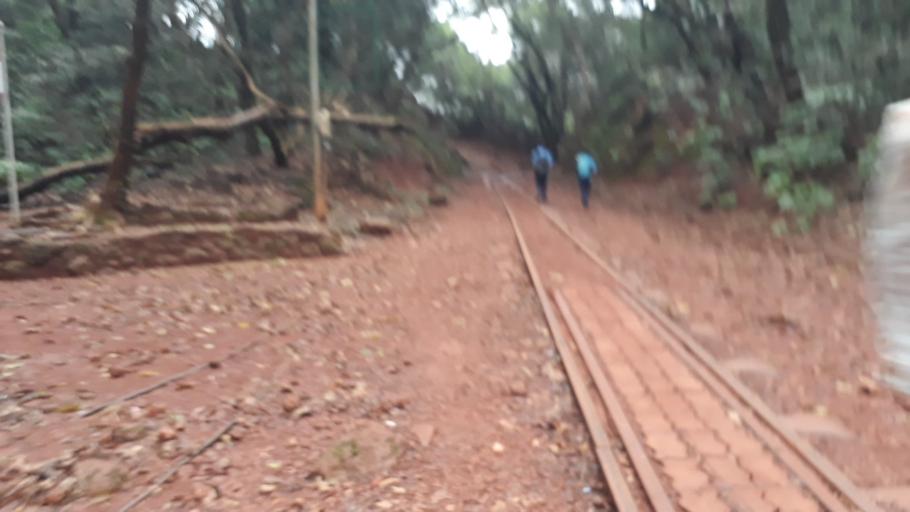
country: IN
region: Maharashtra
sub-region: Raigarh
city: Matheran
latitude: 19.0000
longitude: 73.2802
